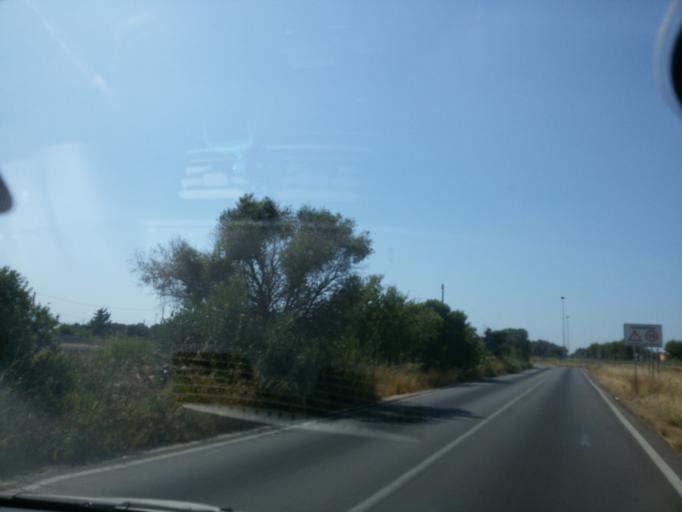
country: IT
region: Apulia
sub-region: Provincia di Lecce
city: Porto Cesareo
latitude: 40.2231
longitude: 17.9403
